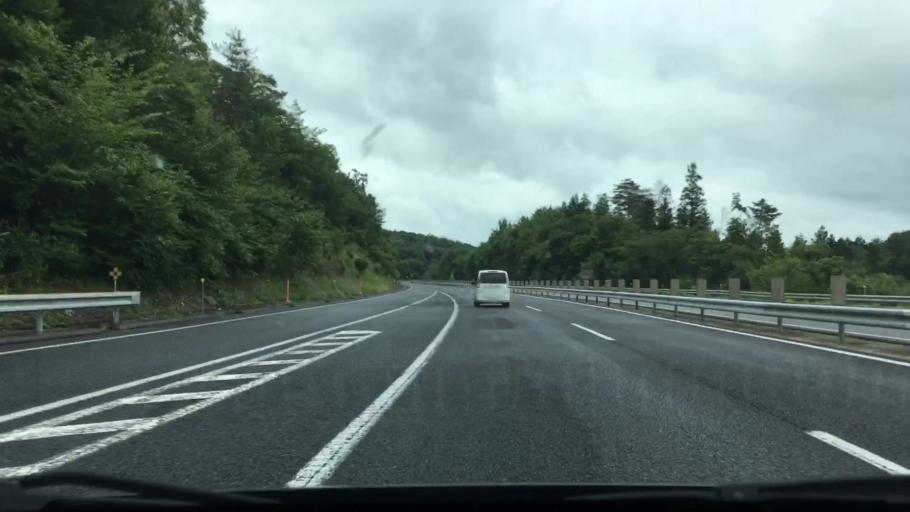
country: JP
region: Hiroshima
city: Miyoshi
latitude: 34.7489
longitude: 132.7239
